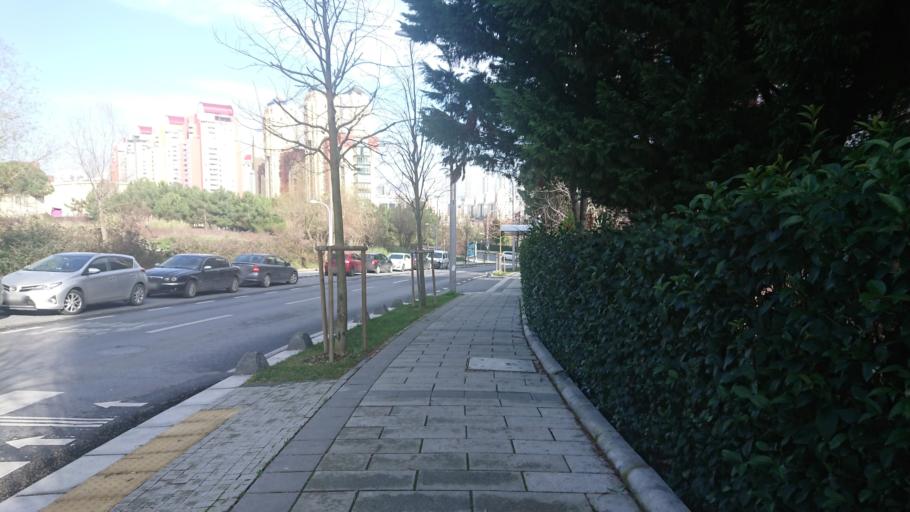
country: TR
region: Istanbul
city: Esenyurt
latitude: 41.0653
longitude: 28.6763
